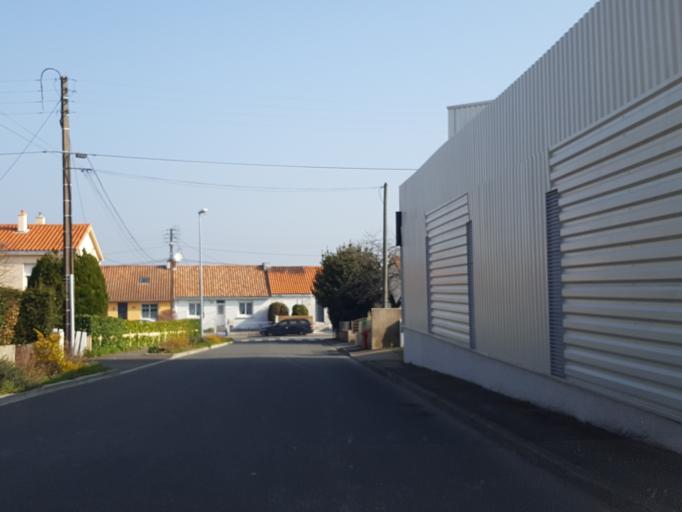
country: FR
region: Pays de la Loire
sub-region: Departement de la Vendee
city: La Roche-sur-Yon
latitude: 46.6666
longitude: -1.4534
